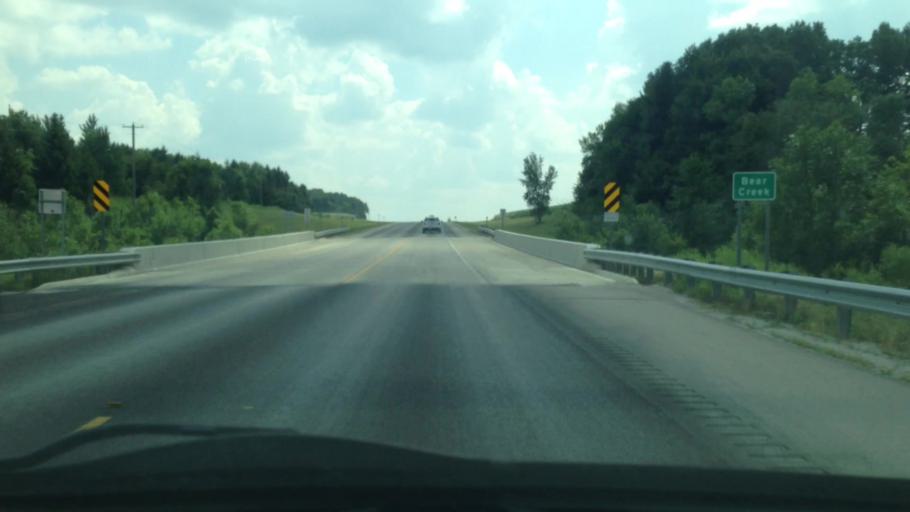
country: US
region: Minnesota
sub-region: Mower County
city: Grand Meadow
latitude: 43.7462
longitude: -92.4793
